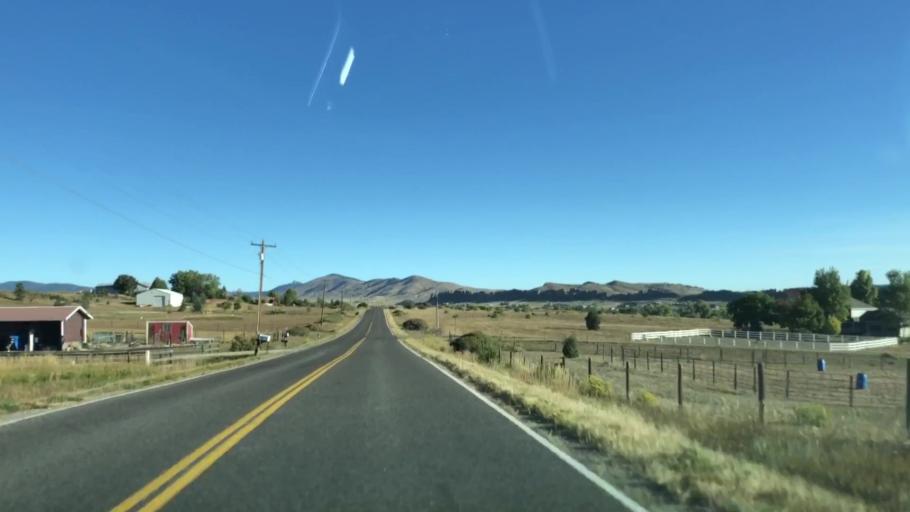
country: US
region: Colorado
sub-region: Larimer County
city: Loveland
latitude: 40.3971
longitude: -105.1683
